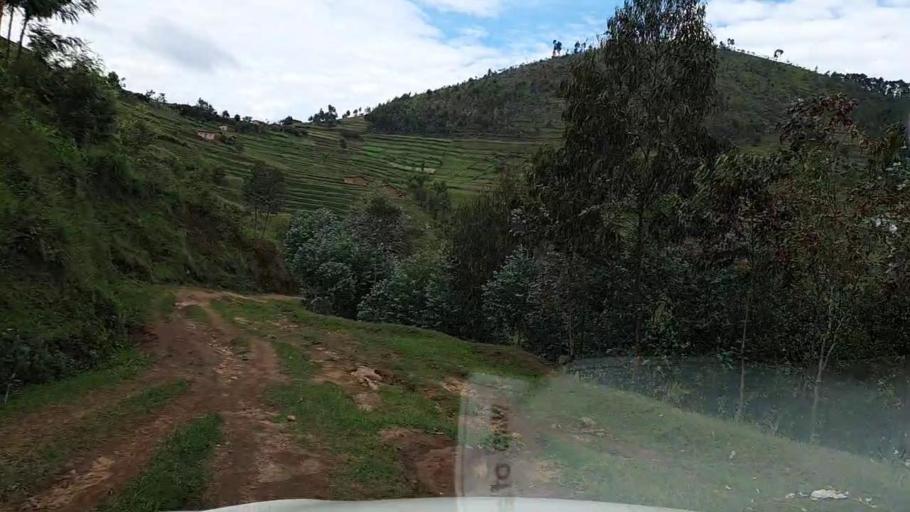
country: RW
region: Southern Province
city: Nzega
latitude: -2.4055
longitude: 29.4985
